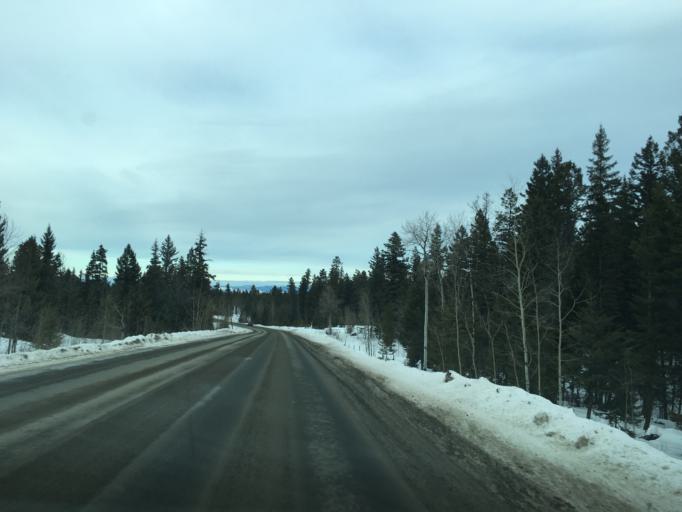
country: CA
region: British Columbia
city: Kamloops
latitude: 50.5579
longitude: -120.4363
